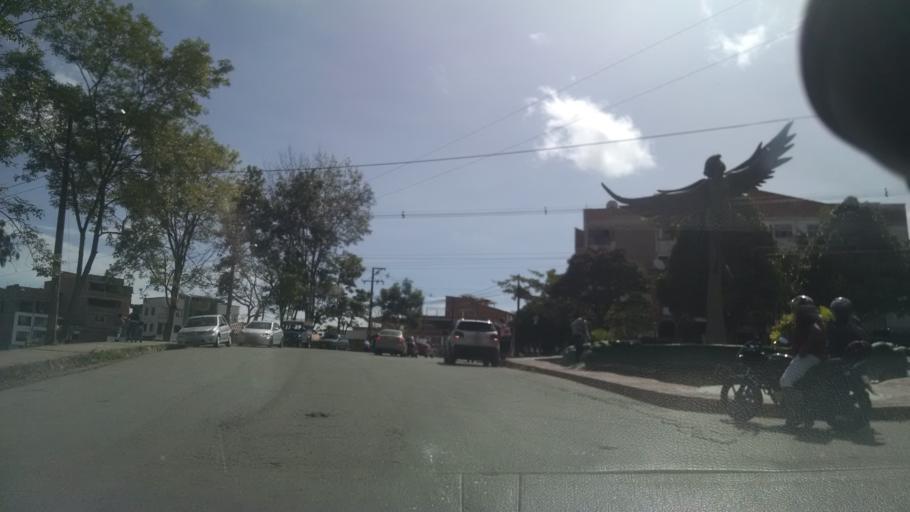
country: CO
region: Antioquia
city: Santuario
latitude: 6.2177
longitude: -75.2439
